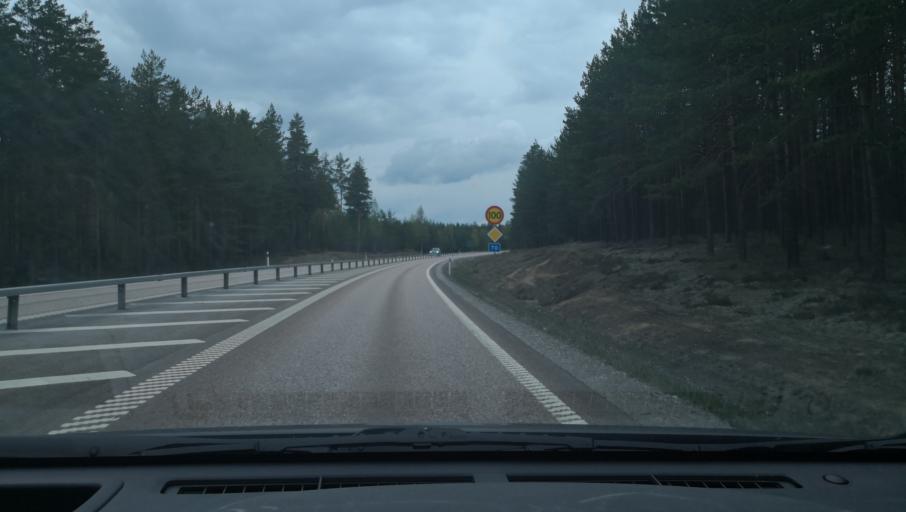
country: SE
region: Dalarna
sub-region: Avesta Kommun
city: Avesta
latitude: 60.0840
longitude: 16.3174
